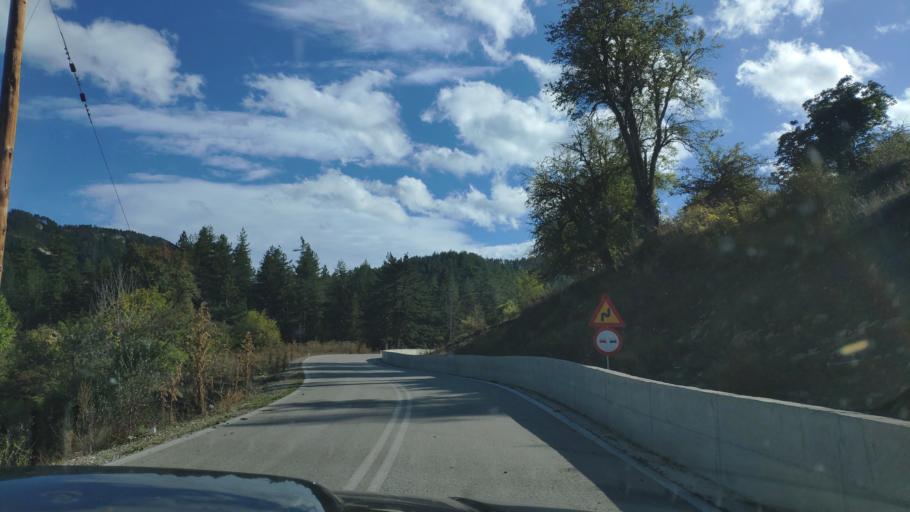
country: AL
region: Korce
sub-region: Rrethi i Devollit
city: Miras
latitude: 40.4003
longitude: 20.8827
